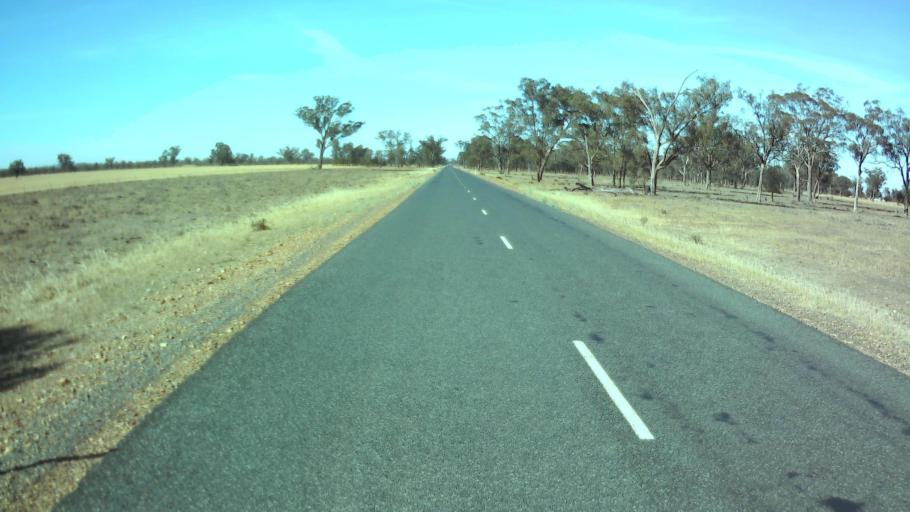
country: AU
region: New South Wales
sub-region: Weddin
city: Grenfell
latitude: -34.0872
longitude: 147.8915
